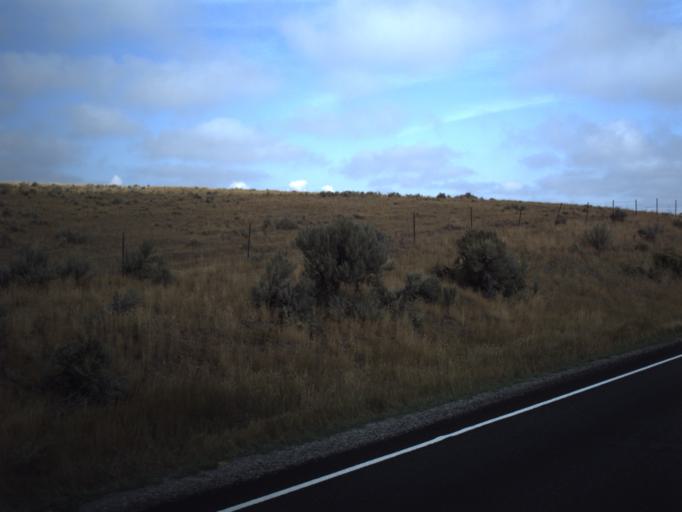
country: US
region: Utah
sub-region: Rich County
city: Randolph
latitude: 41.5404
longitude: -111.1597
